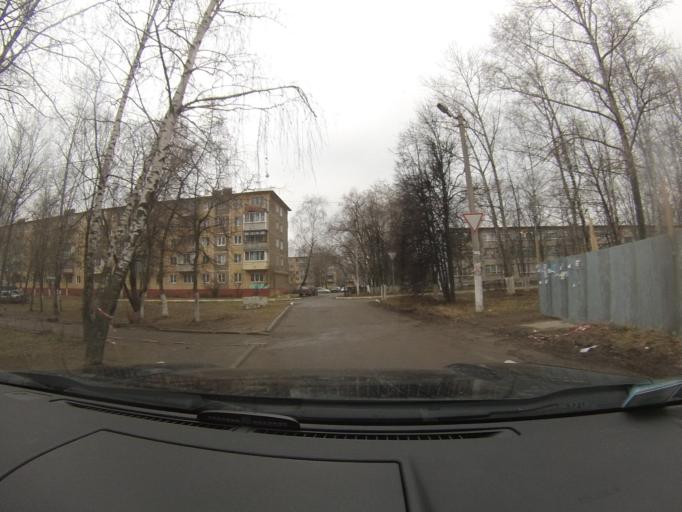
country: RU
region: Moskovskaya
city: Peski
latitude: 55.2708
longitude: 38.7482
